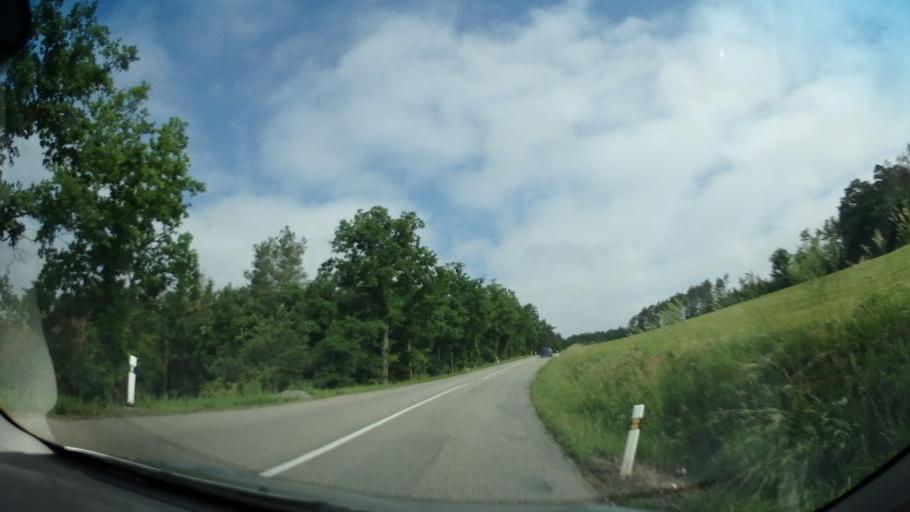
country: CZ
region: South Moravian
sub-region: Okres Brno-Venkov
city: Dolni Loucky
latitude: 49.3678
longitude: 16.3747
